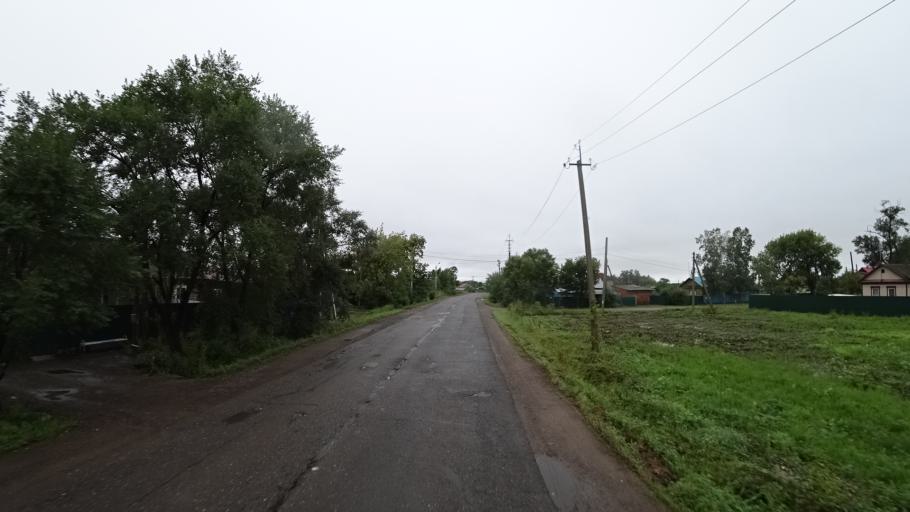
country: RU
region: Primorskiy
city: Monastyrishche
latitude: 44.1994
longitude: 132.4644
